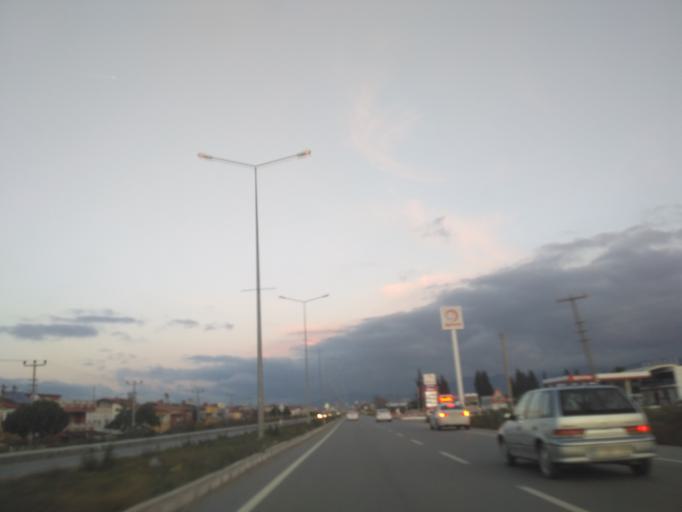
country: TR
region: Balikesir
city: Burhaniye
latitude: 39.4841
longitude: 26.9354
